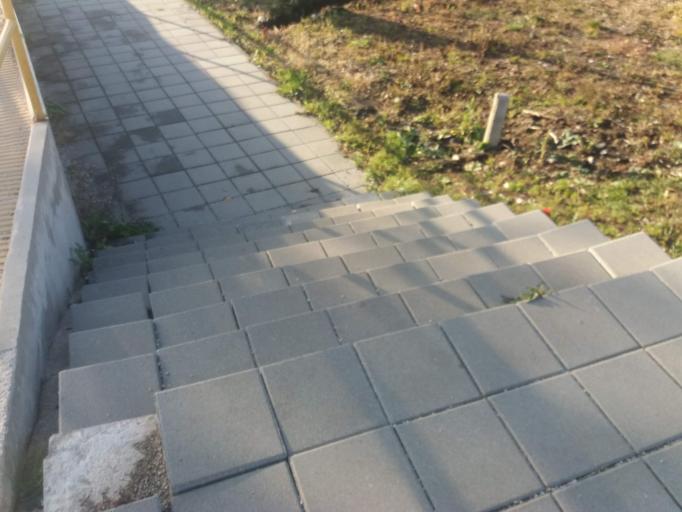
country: RS
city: Zlatibor
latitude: 43.7274
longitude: 19.7057
